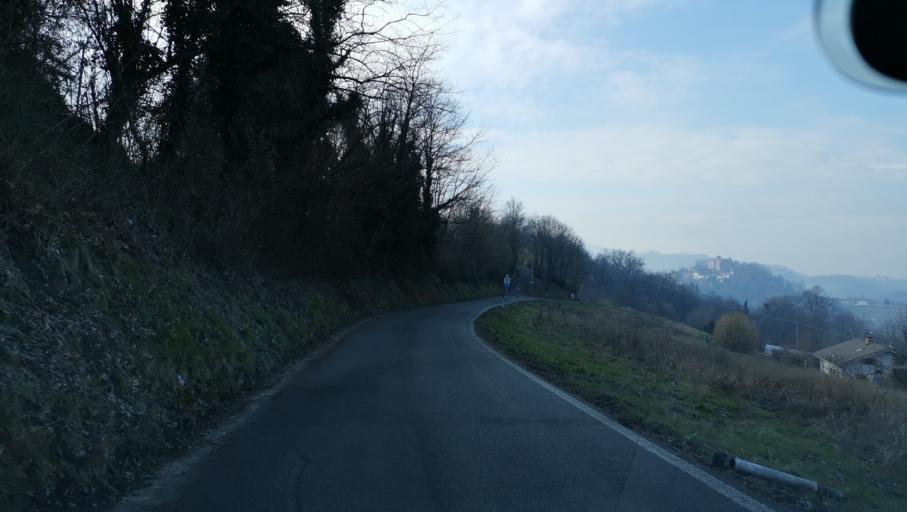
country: IT
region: Piedmont
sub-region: Provincia di Torino
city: Sciolze
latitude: 45.0982
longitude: 7.8577
